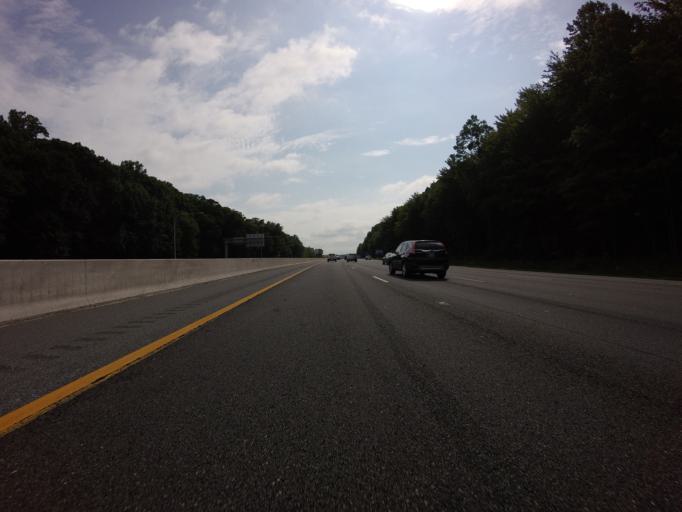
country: US
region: Delaware
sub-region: New Castle County
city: Brookside
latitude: 39.6468
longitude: -75.7569
